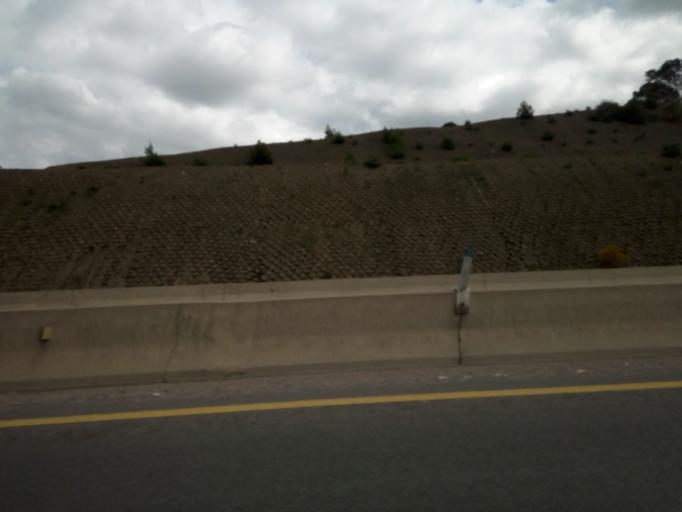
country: DZ
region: Bordj Bou Arreridj
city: Mansourah
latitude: 36.1904
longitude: 4.4285
